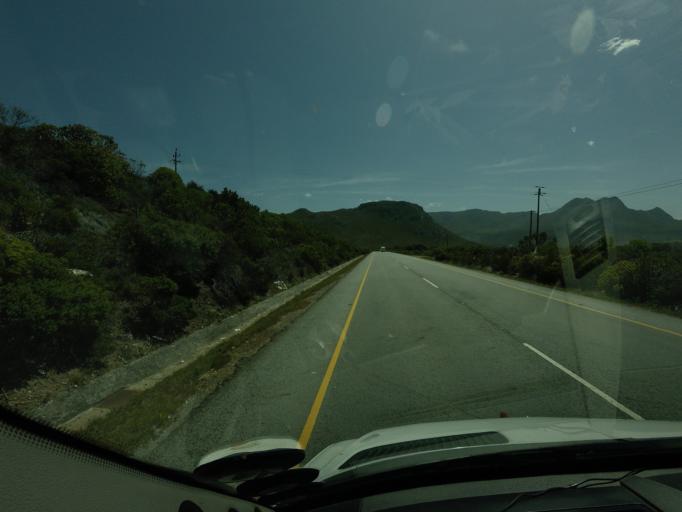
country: ZA
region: Western Cape
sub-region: Overberg District Municipality
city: Grabouw
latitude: -34.3519
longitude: 18.9743
